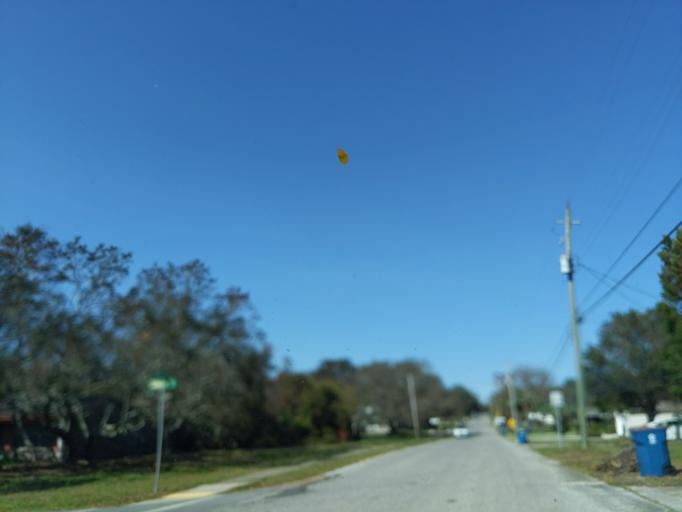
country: US
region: Florida
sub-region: Santa Rosa County
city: Gulf Breeze
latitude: 30.3529
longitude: -87.1880
